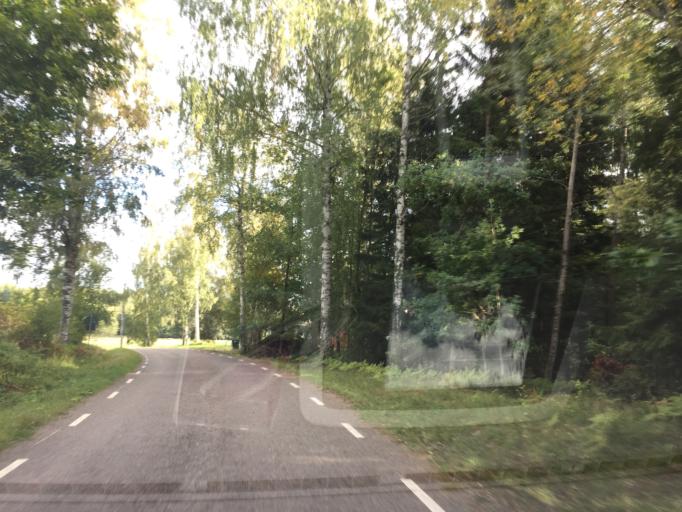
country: SE
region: Soedermanland
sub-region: Vingakers Kommun
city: Vingaker
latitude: 59.0089
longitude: 15.7387
